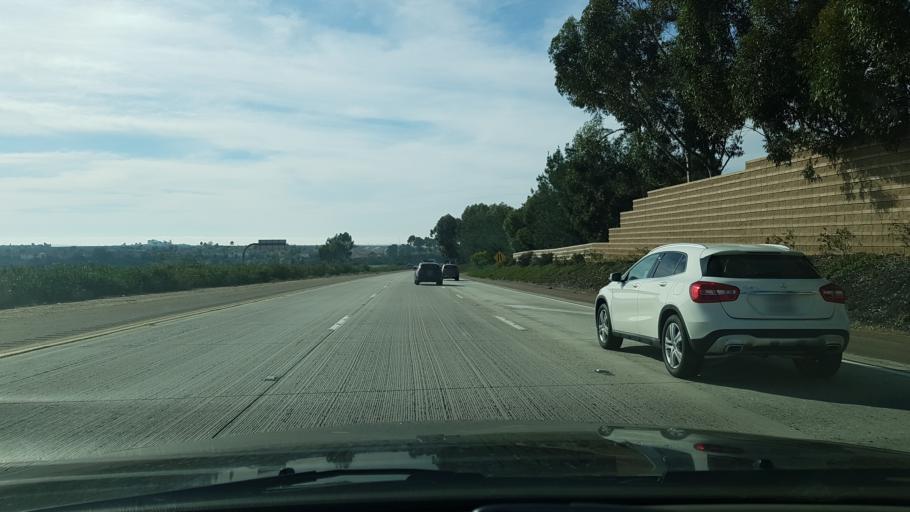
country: US
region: California
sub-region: San Diego County
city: Fairbanks Ranch
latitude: 32.9535
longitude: -117.1377
